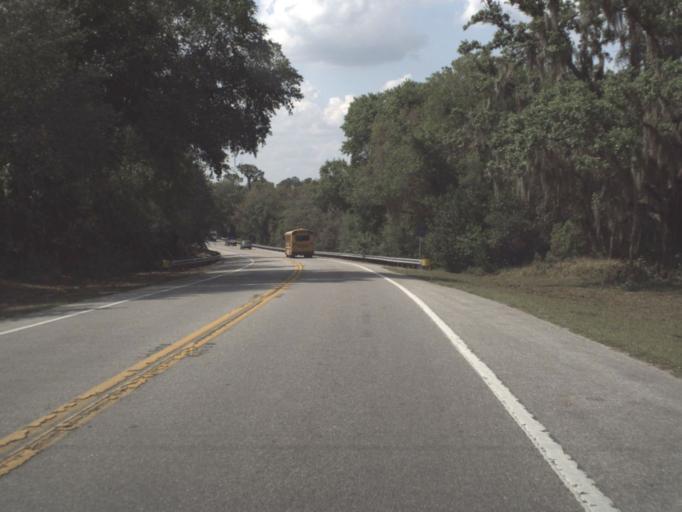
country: US
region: Florida
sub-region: Lake County
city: Howie In The Hills
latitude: 28.7224
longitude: -81.7758
